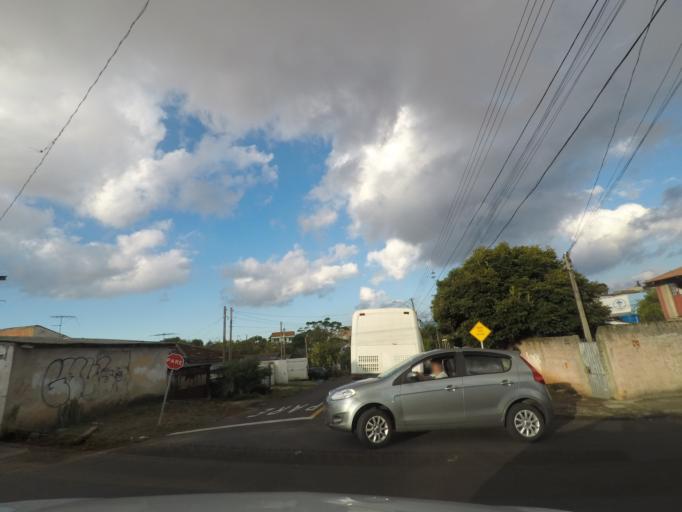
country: BR
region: Parana
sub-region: Sao Jose Dos Pinhais
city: Sao Jose dos Pinhais
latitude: -25.5028
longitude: -49.2595
